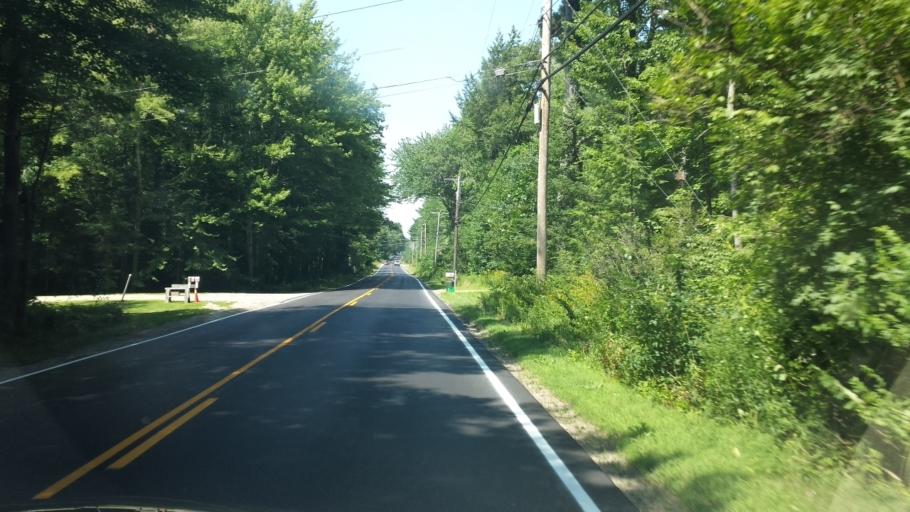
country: US
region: Maine
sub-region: York County
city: Arundel
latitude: 43.3979
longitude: -70.4852
